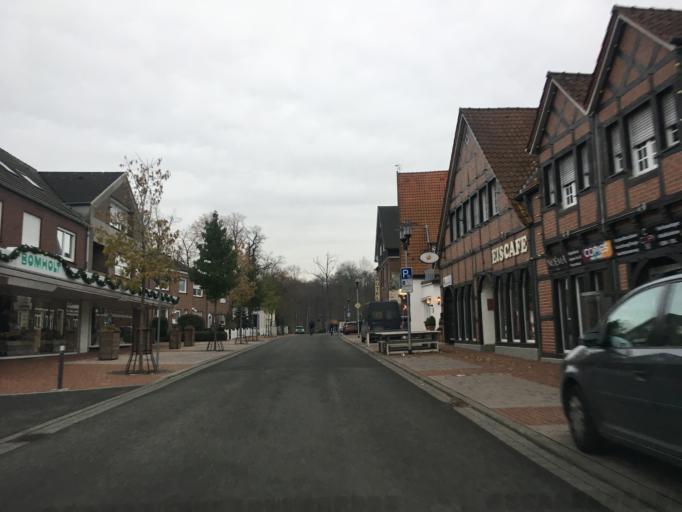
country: DE
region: North Rhine-Westphalia
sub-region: Regierungsbezirk Munster
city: Nordkirchen
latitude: 51.7375
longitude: 7.5271
